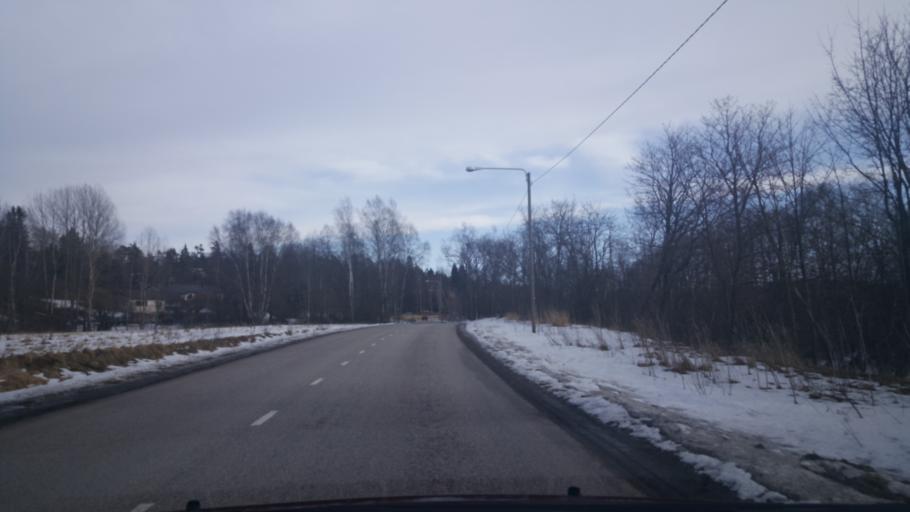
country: FI
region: Uusimaa
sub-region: Helsinki
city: Teekkarikylae
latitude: 60.2929
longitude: 24.8831
